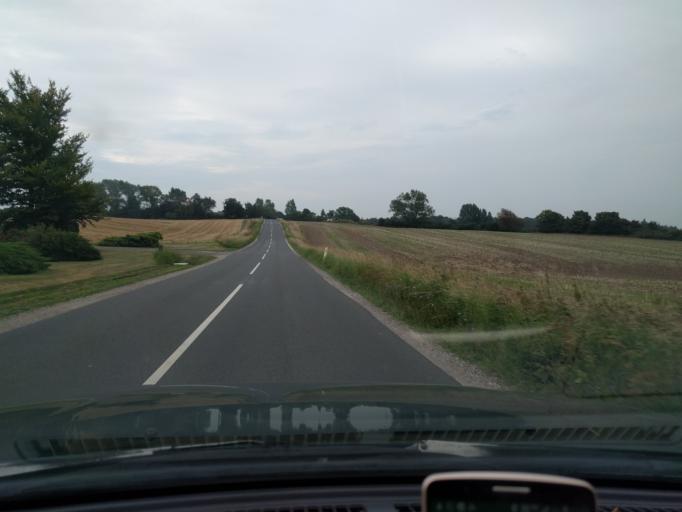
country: DK
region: Zealand
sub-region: Slagelse Kommune
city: Skaelskor
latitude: 55.2950
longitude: 11.2629
